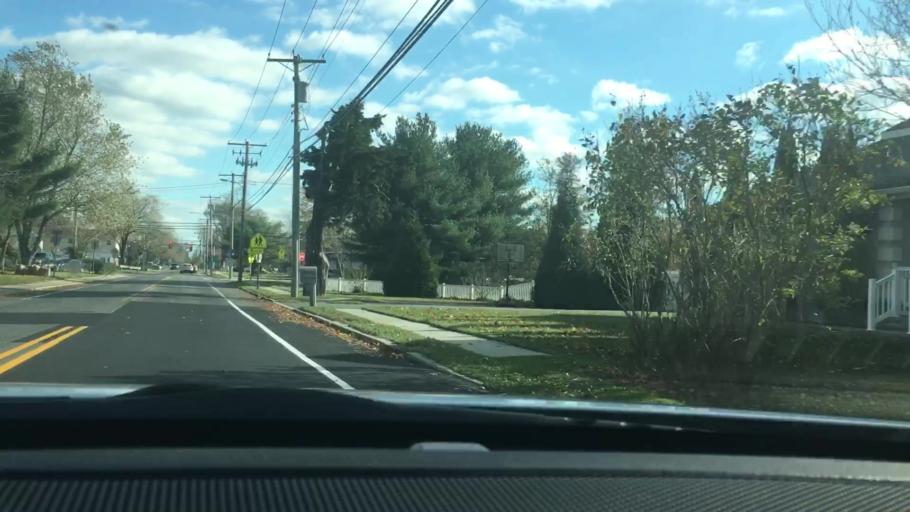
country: US
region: New Jersey
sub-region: Atlantic County
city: Northfield
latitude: 39.3702
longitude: -74.5617
